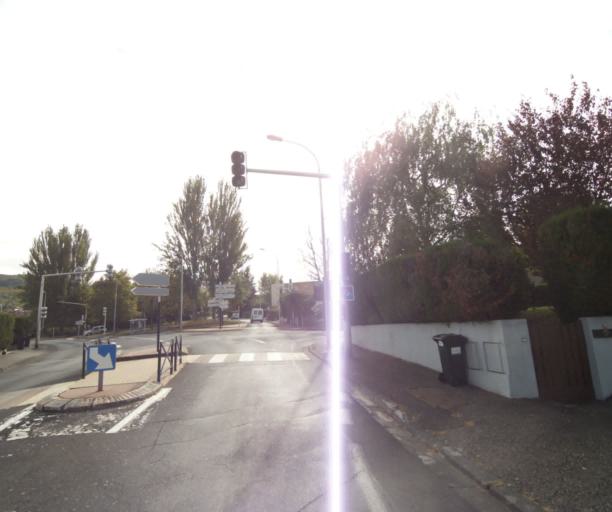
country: FR
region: Auvergne
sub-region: Departement du Puy-de-Dome
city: Romagnat
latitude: 45.7340
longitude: 3.0983
